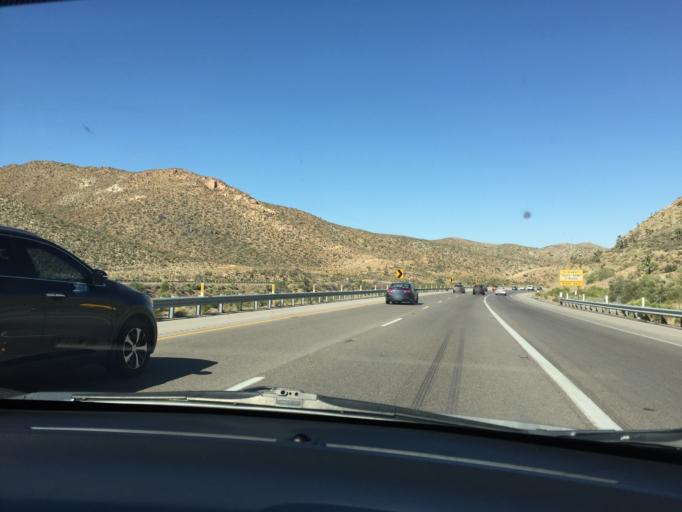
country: US
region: Nevada
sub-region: Clark County
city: Sandy Valley
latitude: 35.4692
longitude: -115.5092
